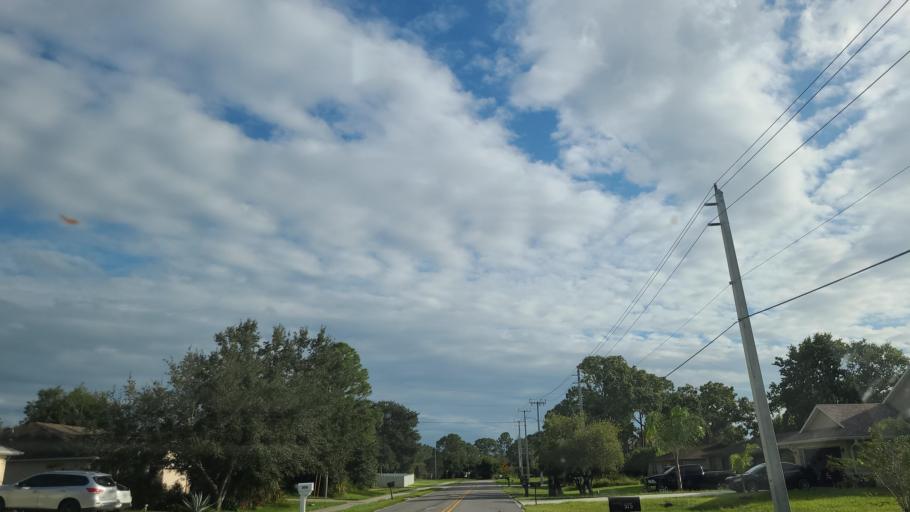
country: US
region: Florida
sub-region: Brevard County
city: June Park
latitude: 28.0080
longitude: -80.6852
